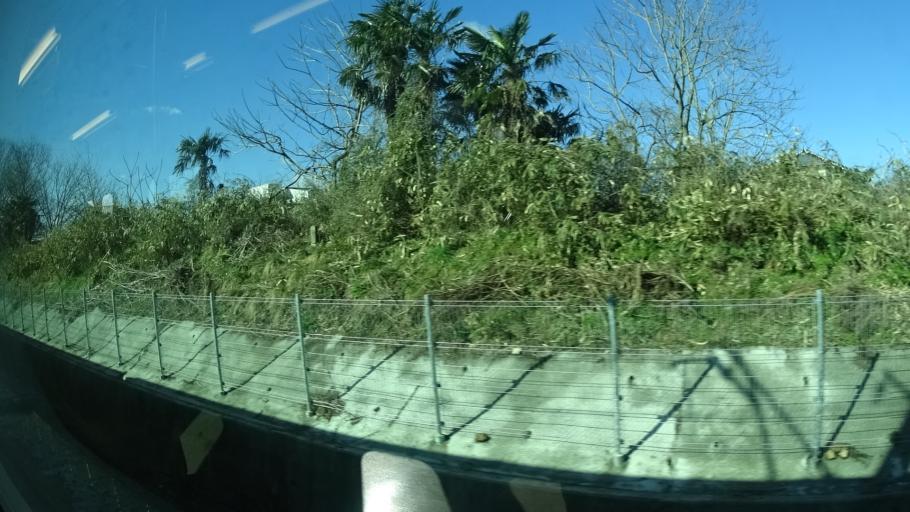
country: JP
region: Fukushima
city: Namie
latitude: 37.4056
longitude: 140.9843
